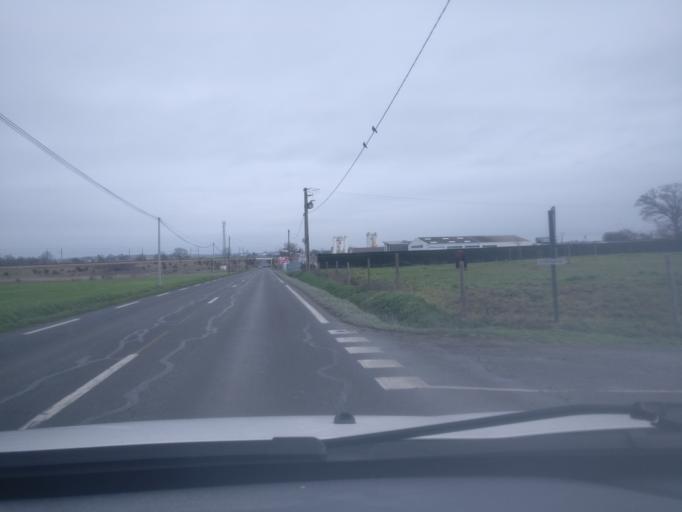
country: FR
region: Brittany
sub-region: Departement d'Ille-et-Vilaine
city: Louvigne-de-Bais
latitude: 48.0591
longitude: -1.3087
